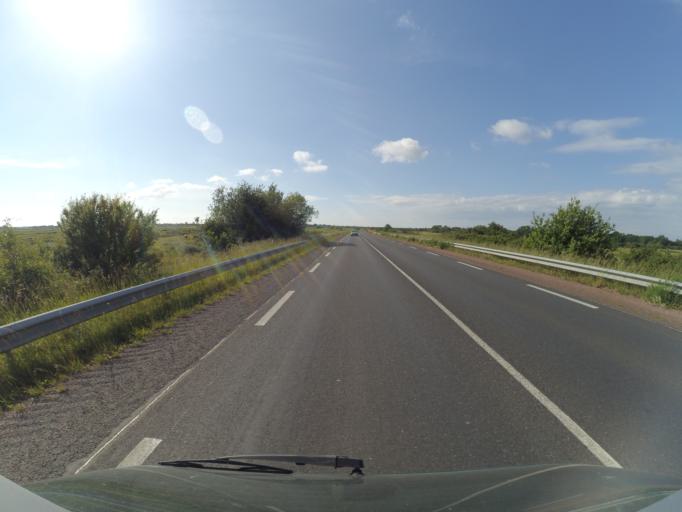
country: FR
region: Poitou-Charentes
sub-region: Departement de la Charente-Maritime
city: Saint-Agnant
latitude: 45.8557
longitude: -0.9633
